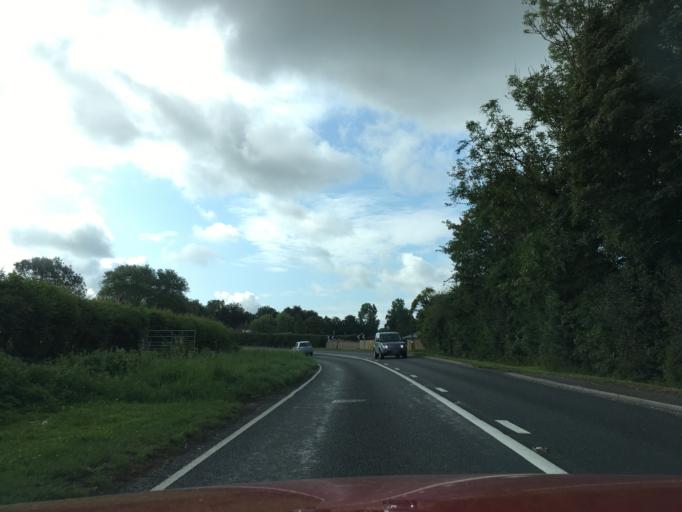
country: GB
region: England
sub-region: Hampshire
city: Swanmore
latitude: 50.9256
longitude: -1.2010
